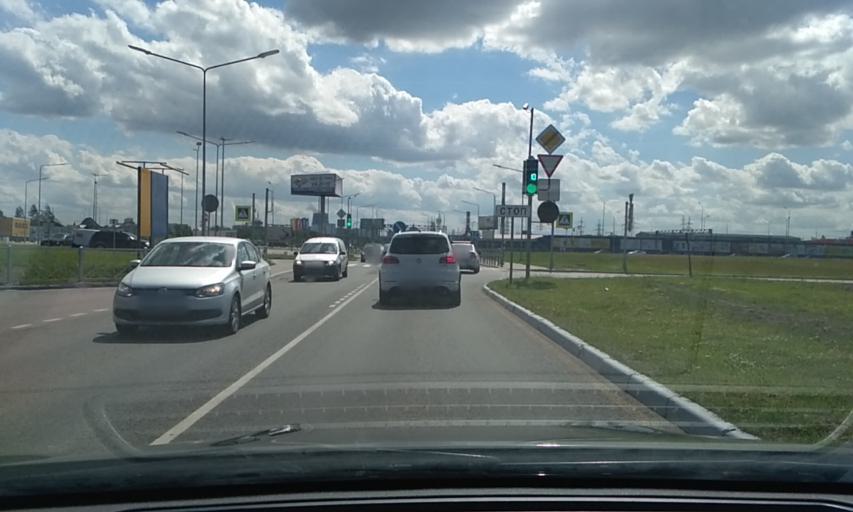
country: RU
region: Leningrad
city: Rybatskoye
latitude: 59.8917
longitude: 30.5087
